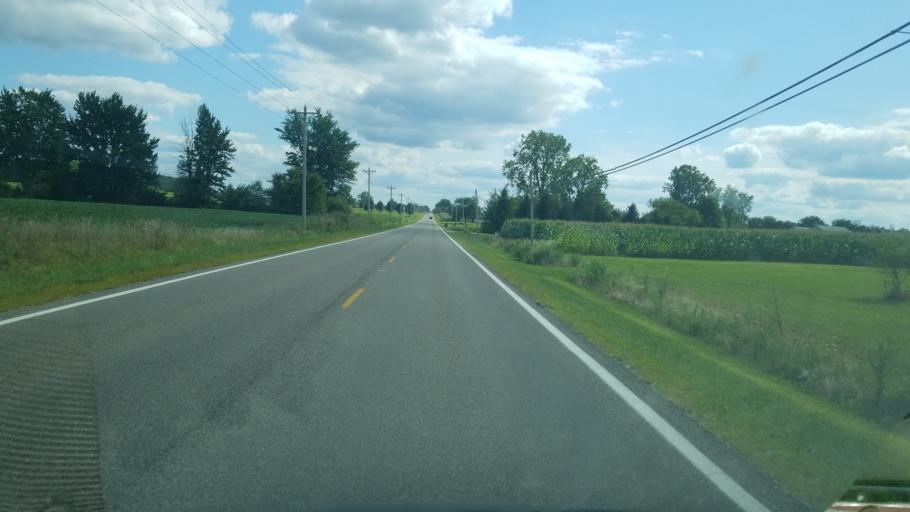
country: US
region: Ohio
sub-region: Logan County
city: Lakeview
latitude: 40.6291
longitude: -83.9756
